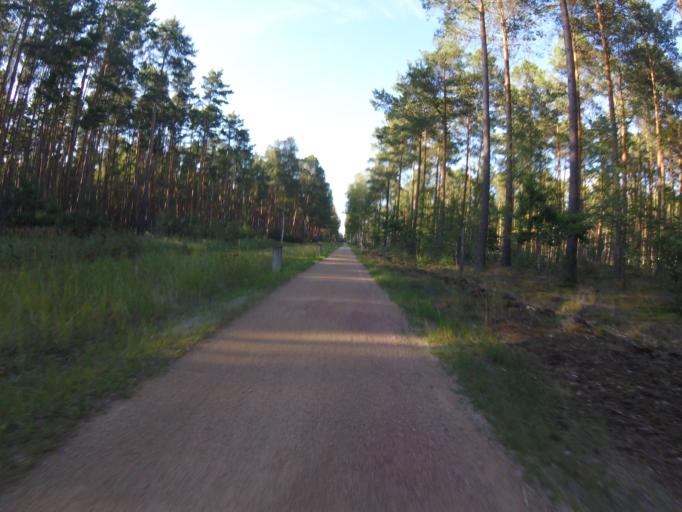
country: DE
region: Brandenburg
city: Halbe
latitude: 52.1901
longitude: 13.7611
